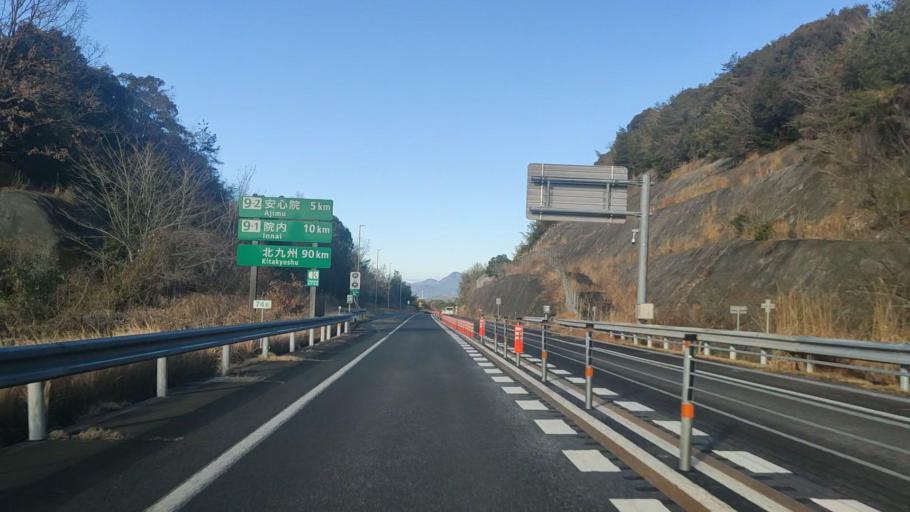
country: JP
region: Oita
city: Hiji
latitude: 33.4314
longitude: 131.4182
